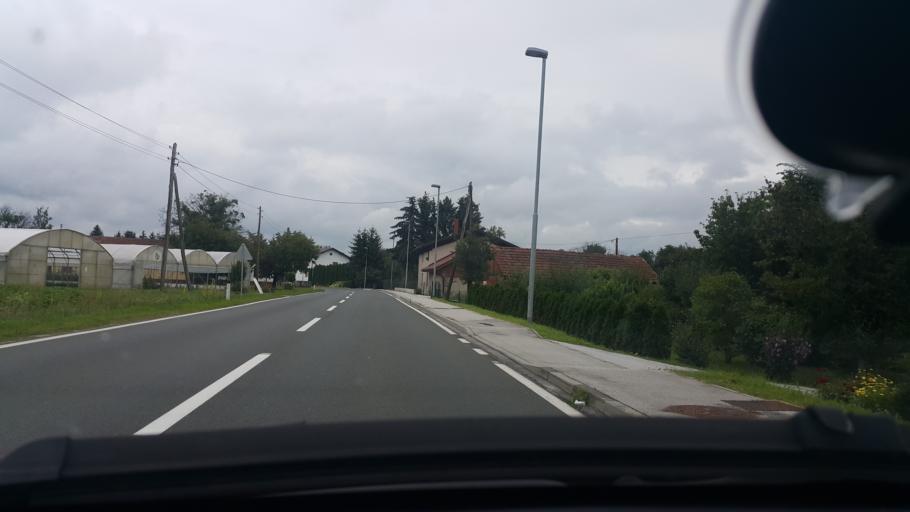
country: SI
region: Zavrc
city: Zavrc
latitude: 46.4147
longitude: 16.0904
